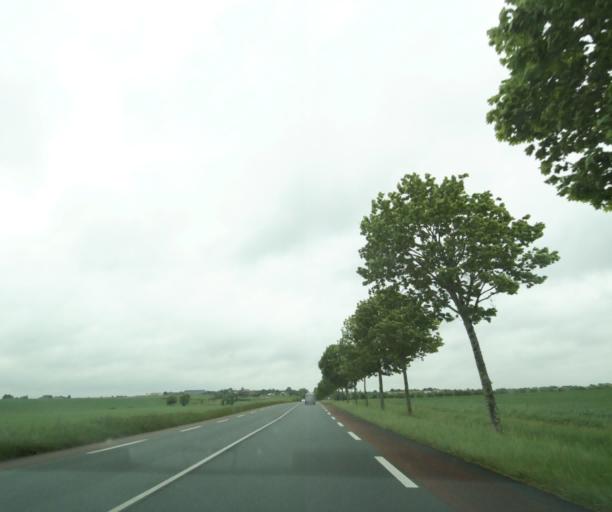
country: FR
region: Poitou-Charentes
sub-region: Departement de la Charente-Maritime
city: Les Gonds
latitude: 45.6615
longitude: -0.5936
